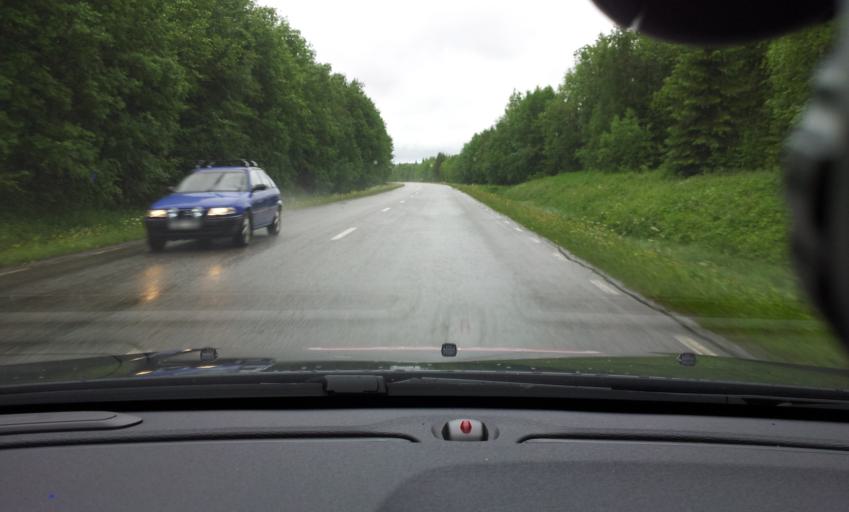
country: SE
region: Jaemtland
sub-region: Krokoms Kommun
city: Krokom
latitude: 63.3793
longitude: 14.5063
